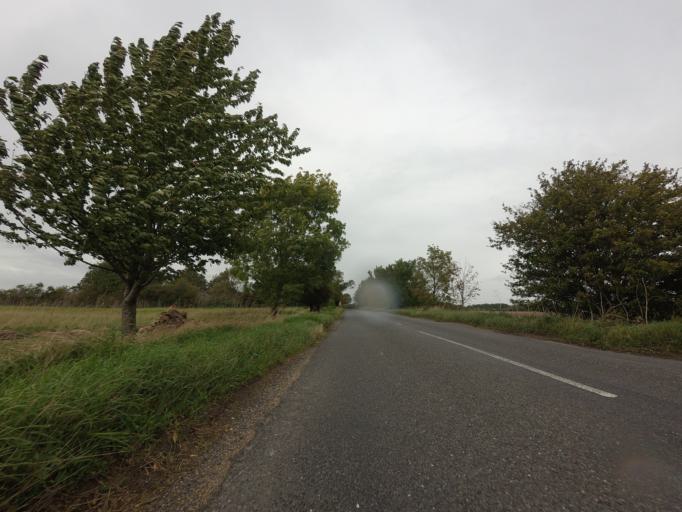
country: GB
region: England
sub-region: Cambridgeshire
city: Harston
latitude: 52.0825
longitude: 0.0799
